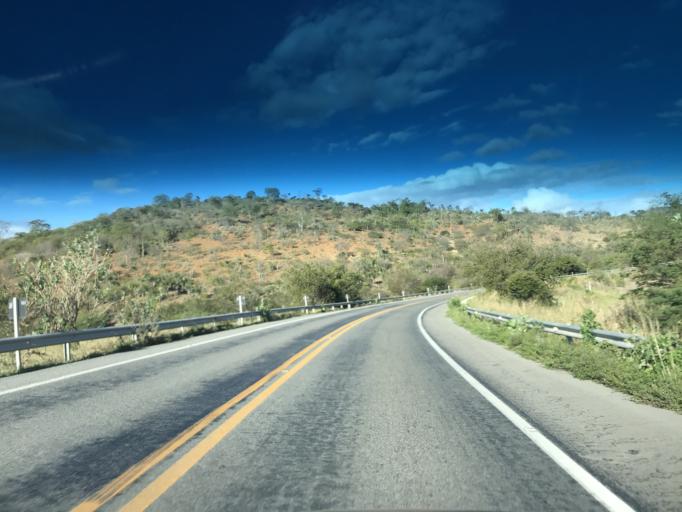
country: BR
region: Bahia
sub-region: Itaberaba
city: Itaberaba
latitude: -12.5085
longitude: -40.4477
